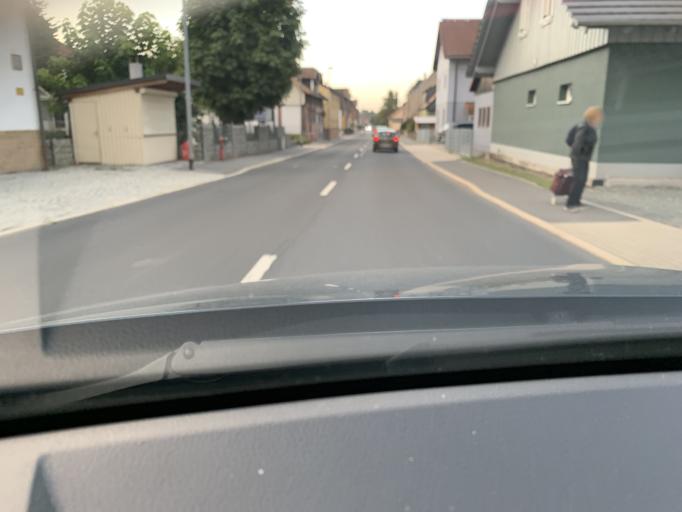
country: DE
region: Bavaria
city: Foritz
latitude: 50.3636
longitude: 11.2077
